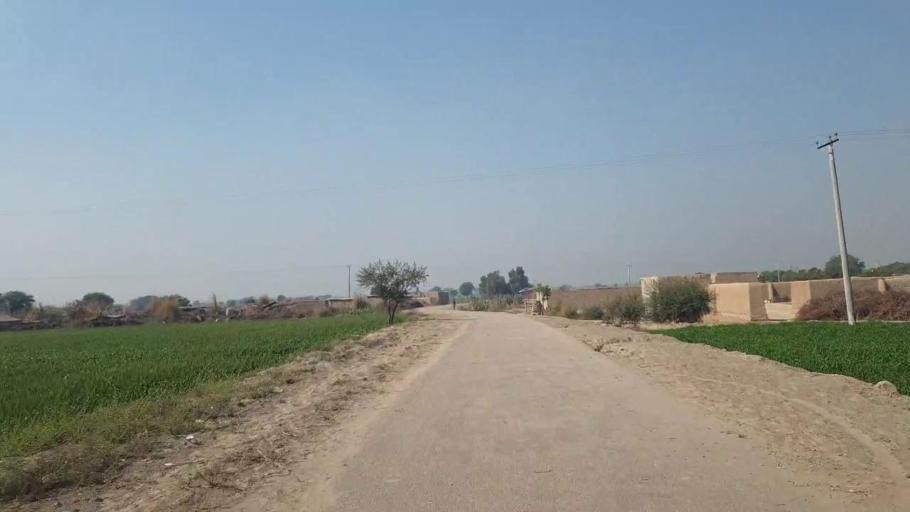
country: PK
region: Sindh
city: Shahpur Chakar
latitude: 26.1109
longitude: 68.6026
